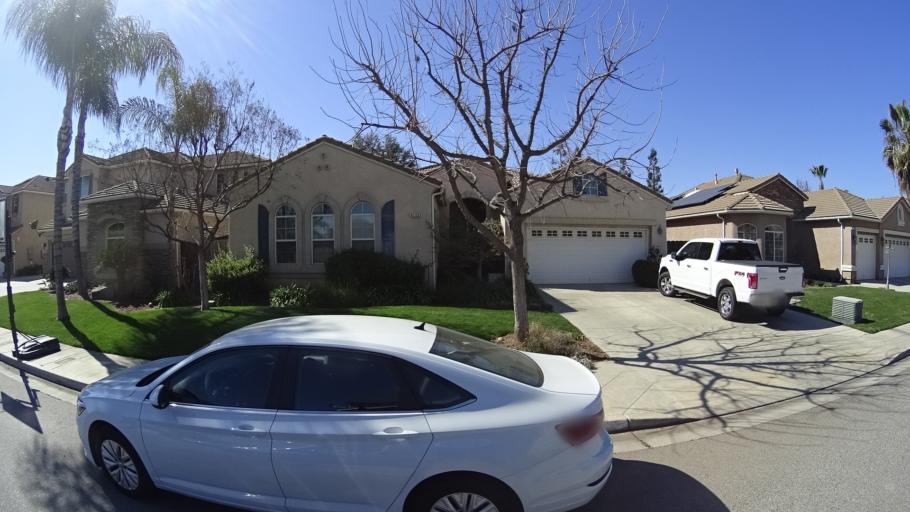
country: US
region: California
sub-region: Fresno County
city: Clovis
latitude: 36.8542
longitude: -119.7338
